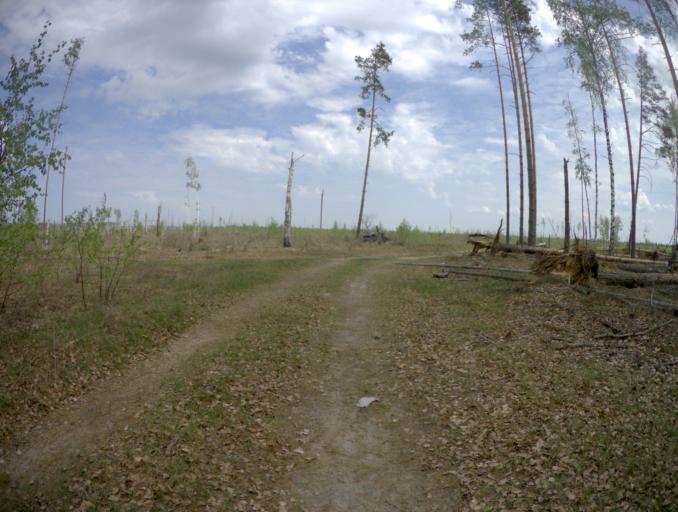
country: RU
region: Ivanovo
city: Talitsy
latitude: 56.4896
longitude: 42.1747
